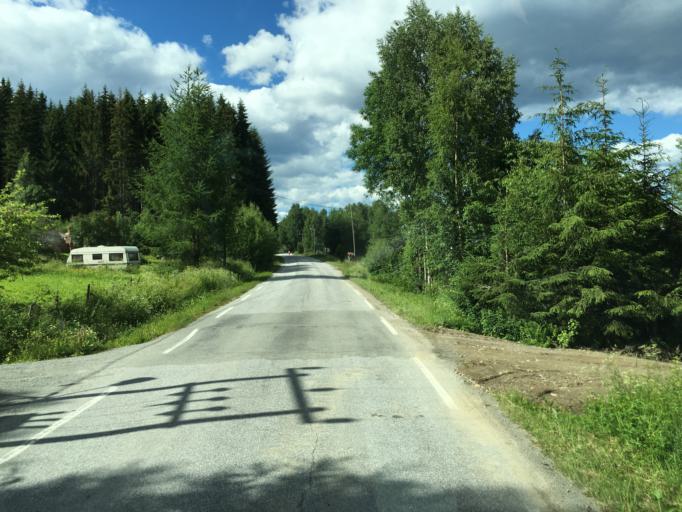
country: NO
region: Oppland
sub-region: Sondre Land
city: Hov
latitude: 60.6810
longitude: 10.3111
